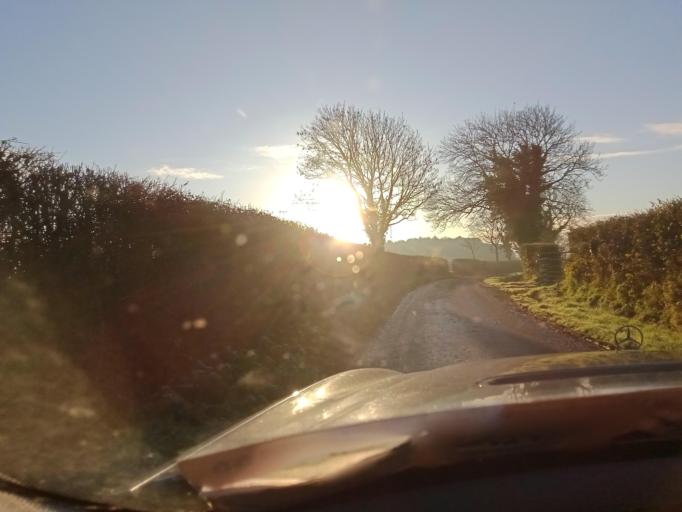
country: IE
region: Leinster
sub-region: Kilkenny
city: Callan
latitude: 52.5366
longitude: -7.4306
